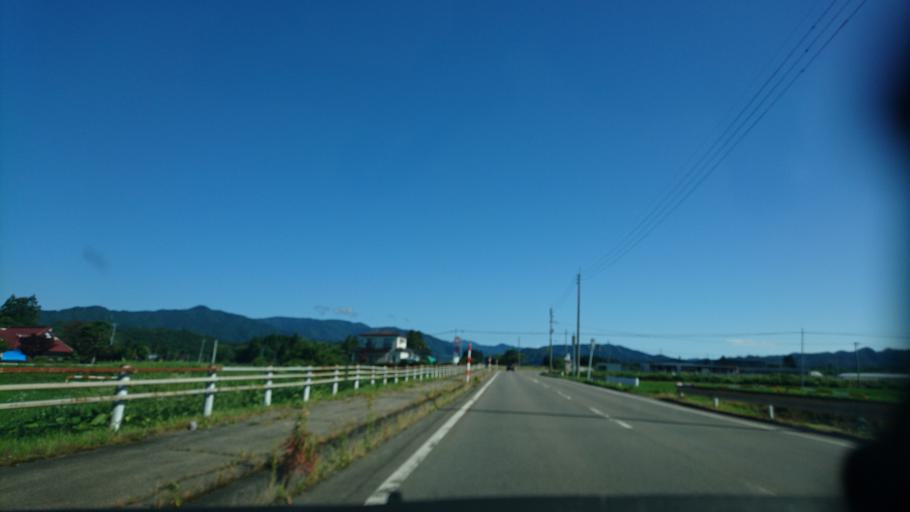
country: JP
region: Akita
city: Kakunodatemachi
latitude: 39.6313
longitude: 140.5703
